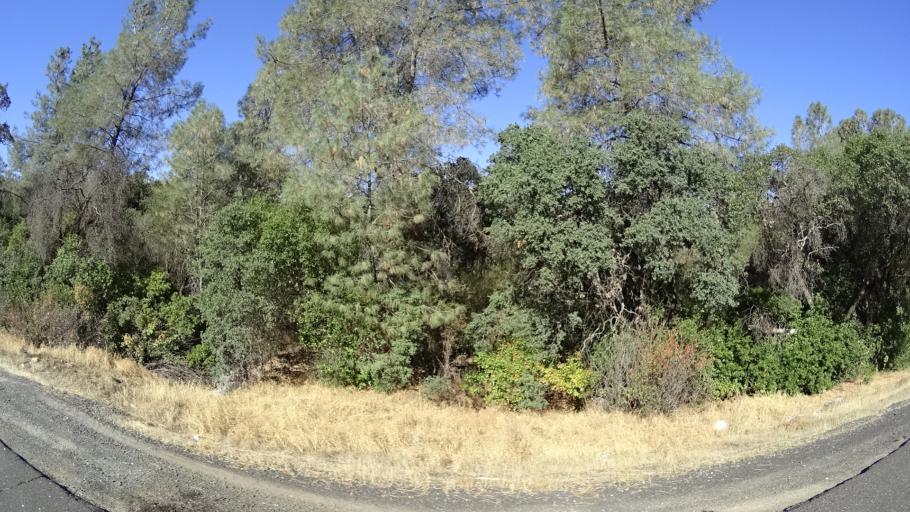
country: US
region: California
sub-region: Tuolumne County
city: Columbia
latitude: 38.0484
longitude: -120.4699
